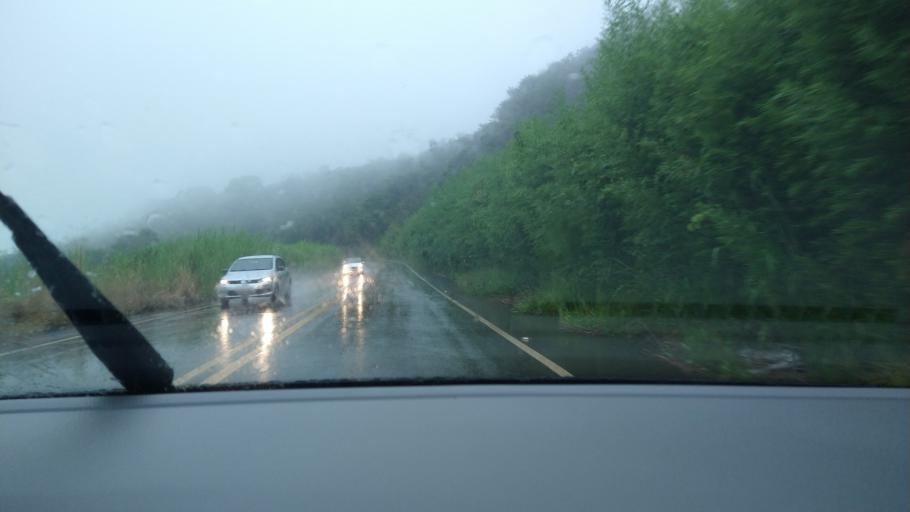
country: BR
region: Minas Gerais
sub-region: Ponte Nova
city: Ponte Nova
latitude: -20.5607
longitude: -42.8721
